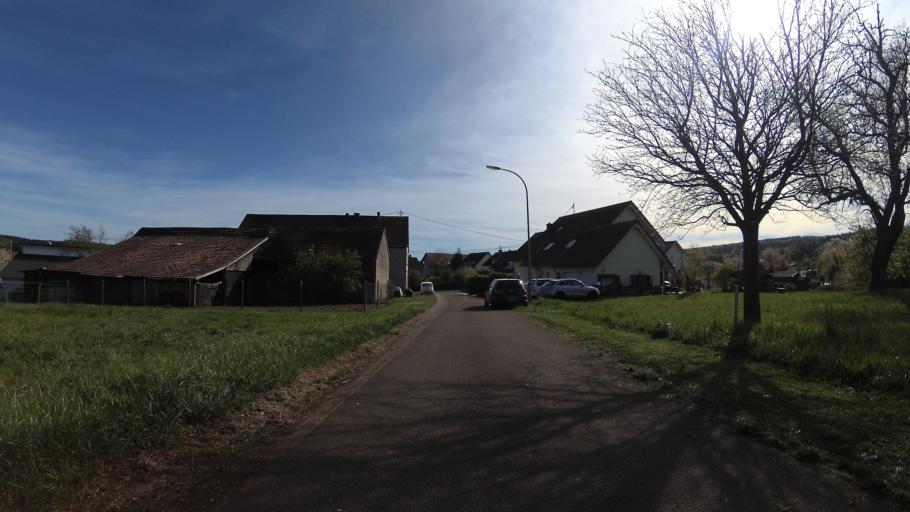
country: DE
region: Saarland
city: Mainzweiler
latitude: 49.4394
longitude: 7.1223
